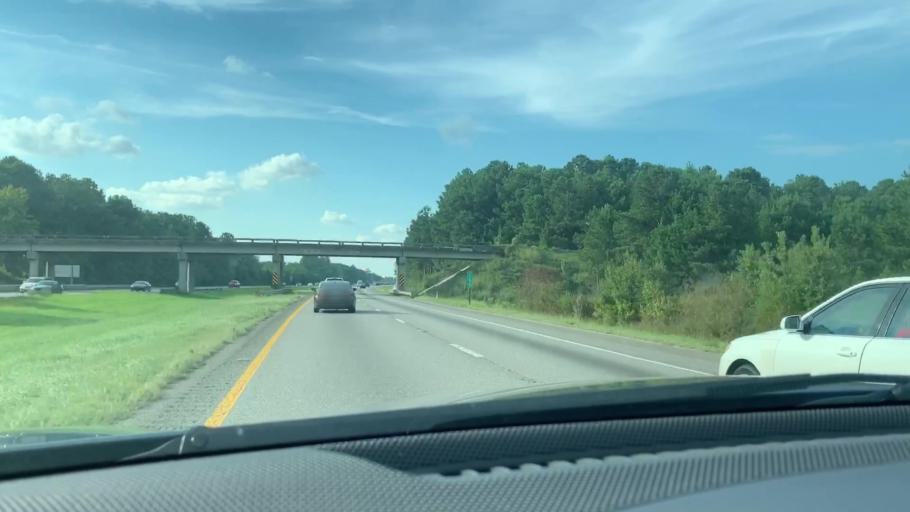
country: US
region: South Carolina
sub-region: Orangeburg County
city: Brookdale
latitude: 33.4499
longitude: -80.7202
